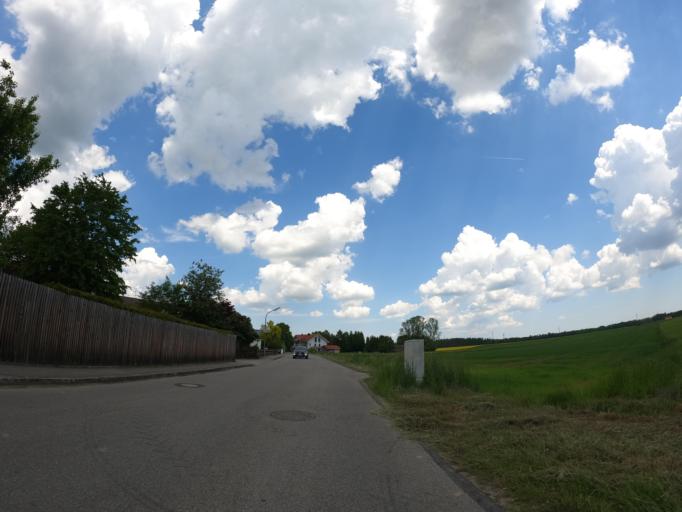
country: DE
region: Bavaria
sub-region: Upper Bavaria
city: Sauerlach
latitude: 47.9799
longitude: 11.6529
